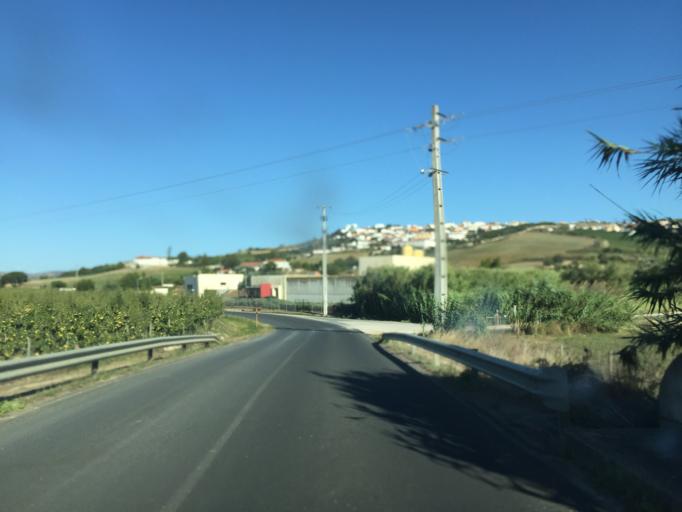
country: PT
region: Lisbon
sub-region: Torres Vedras
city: Torres Vedras
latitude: 39.0948
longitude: -9.2882
